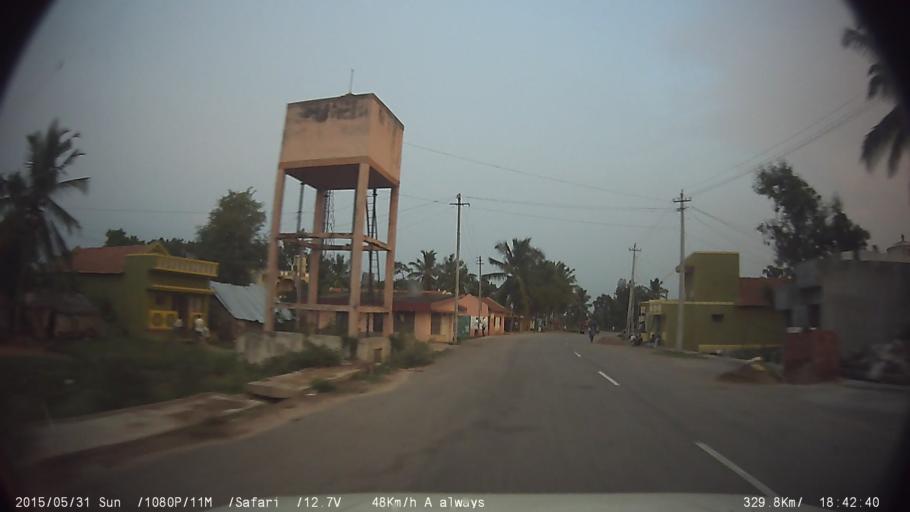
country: IN
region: Karnataka
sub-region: Mysore
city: Tirumakudal Narsipur
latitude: 12.1528
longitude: 76.8020
